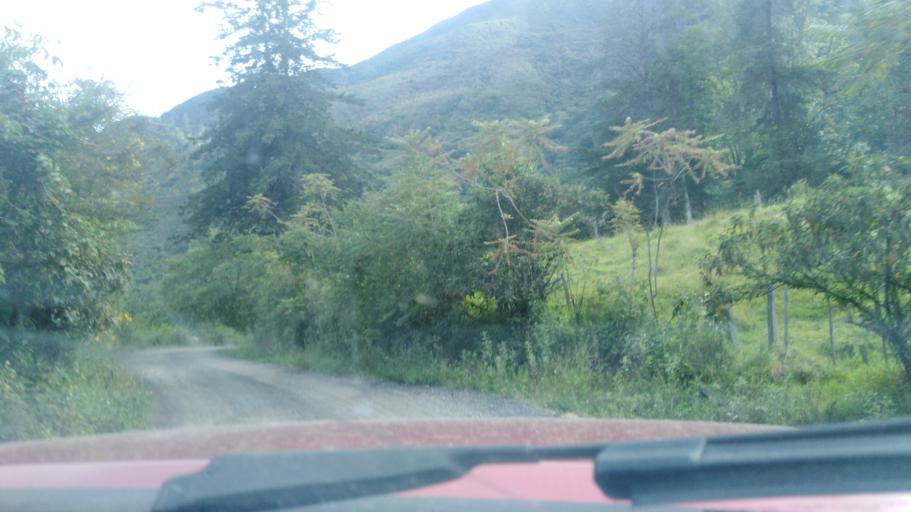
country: CO
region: Boyaca
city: San Mateo
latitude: 6.4218
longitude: -72.5617
